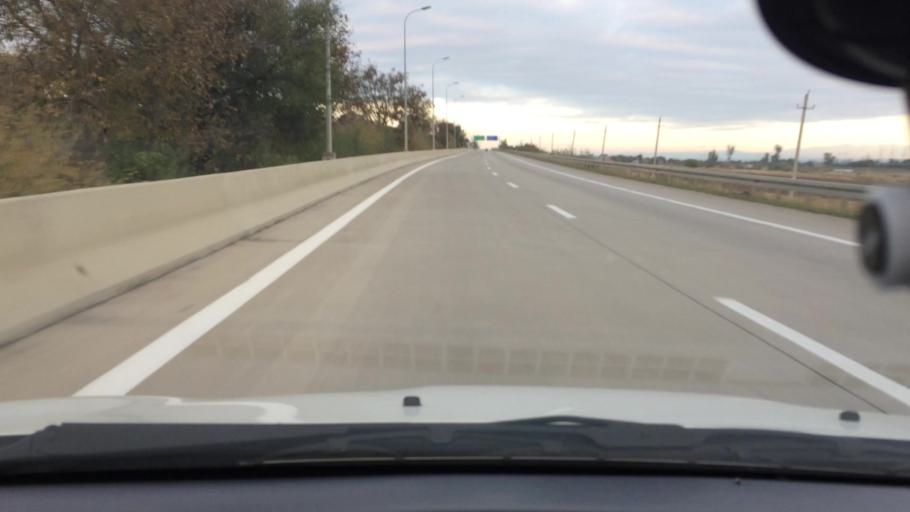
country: GE
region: Shida Kartli
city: Kaspi
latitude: 42.0211
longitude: 44.2986
